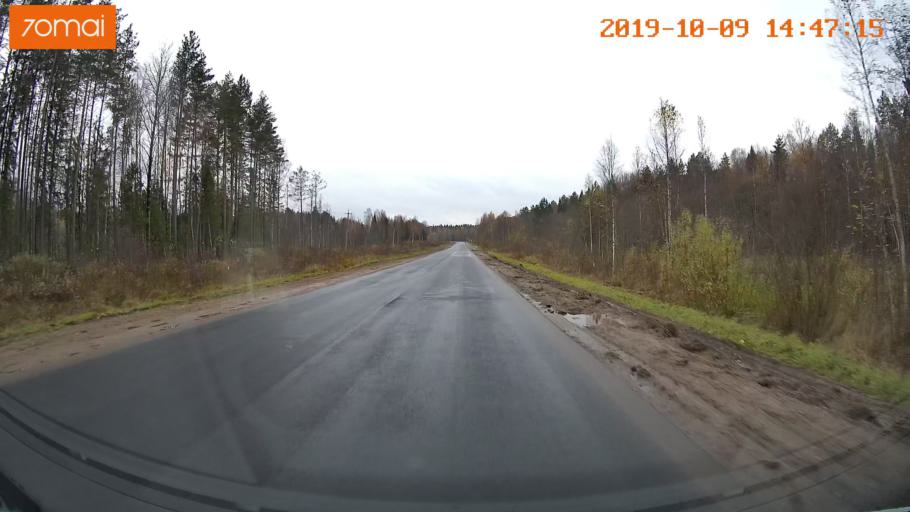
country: RU
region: Kostroma
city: Buy
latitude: 58.4204
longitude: 41.5734
